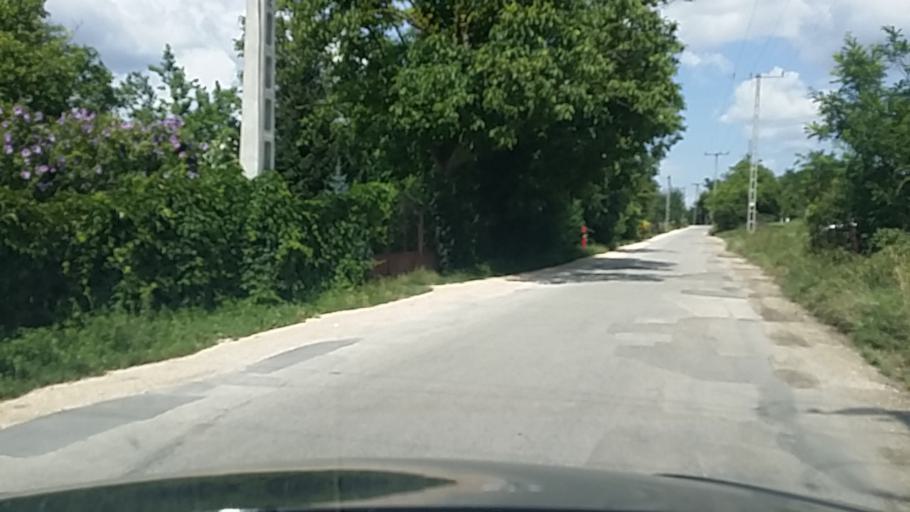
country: HU
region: Bacs-Kiskun
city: Kecskemet
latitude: 46.9203
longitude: 19.6533
